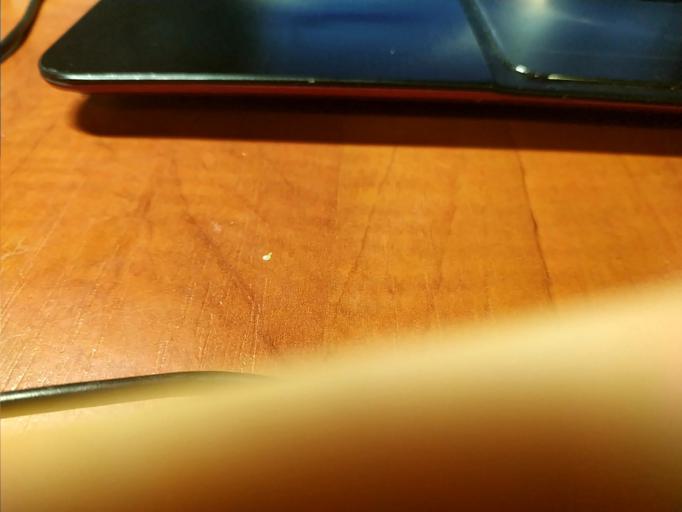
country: RU
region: Tverskaya
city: Likhoslavl'
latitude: 56.9883
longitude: 35.6203
